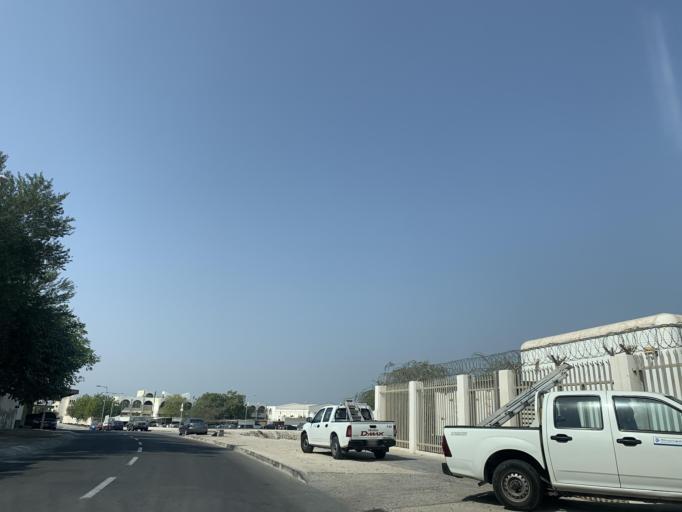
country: BH
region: Central Governorate
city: Madinat Hamad
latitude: 26.1315
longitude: 50.5045
